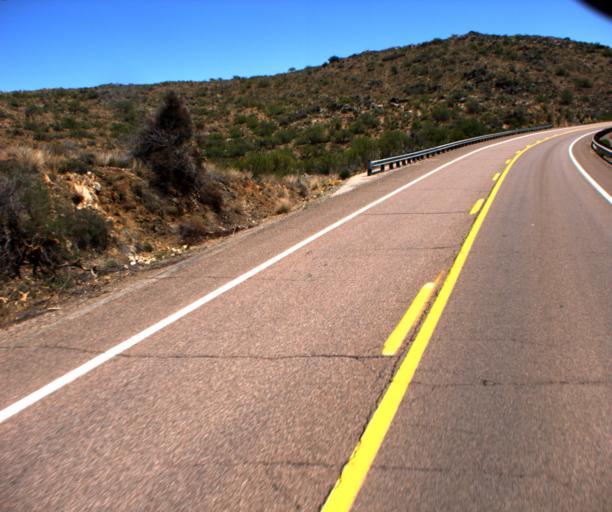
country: US
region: Arizona
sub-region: Yavapai County
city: Bagdad
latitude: 34.5562
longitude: -113.1568
